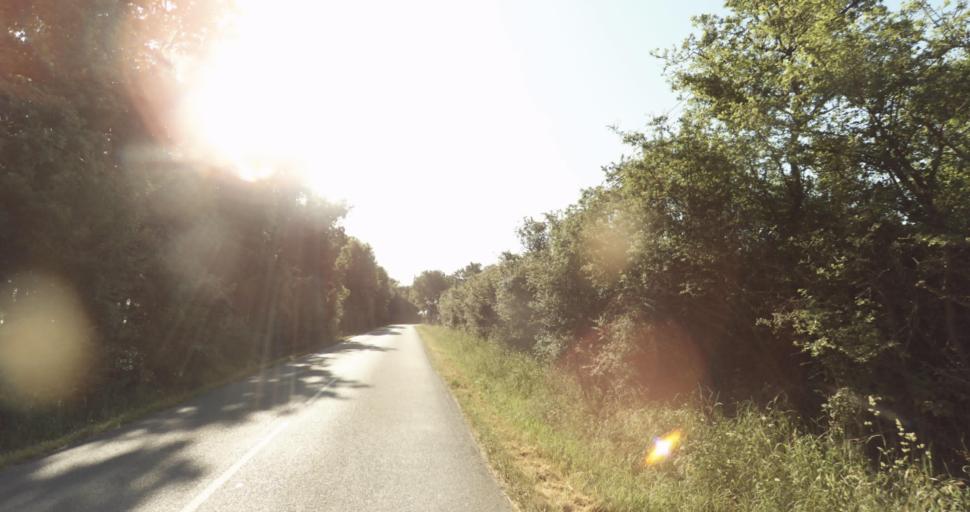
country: FR
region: Midi-Pyrenees
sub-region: Departement de la Haute-Garonne
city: Leguevin
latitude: 43.5780
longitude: 1.2256
